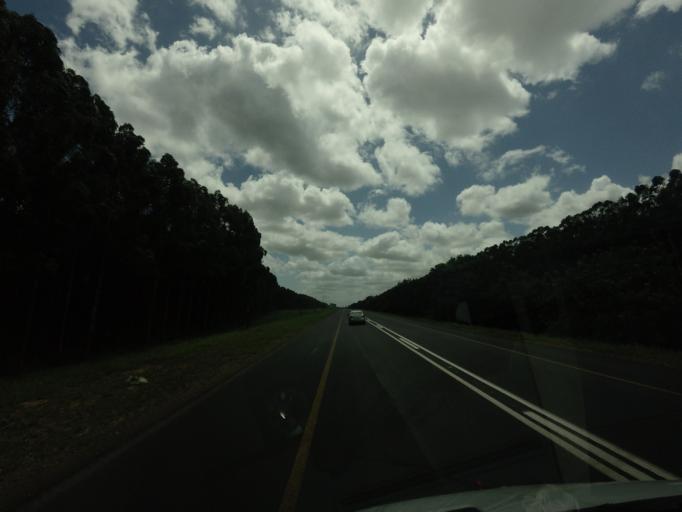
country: ZA
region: KwaZulu-Natal
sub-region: uThungulu District Municipality
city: KwaMbonambi
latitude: -28.5361
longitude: 32.1311
